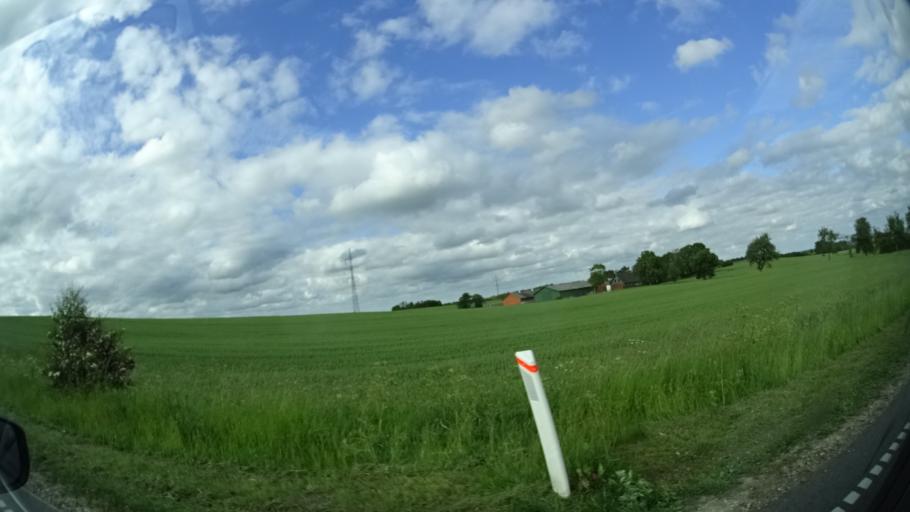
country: DK
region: Central Jutland
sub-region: Syddjurs Kommune
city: Ronde
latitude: 56.3177
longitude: 10.4212
